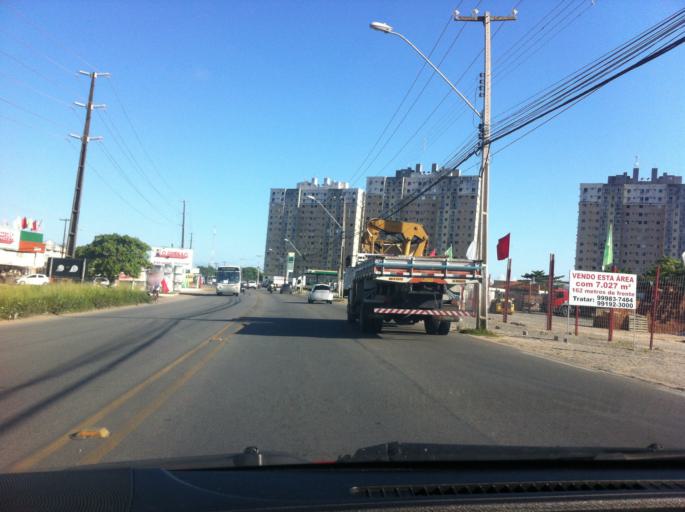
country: BR
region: Alagoas
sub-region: Maceio
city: Maceio
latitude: -9.5839
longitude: -35.7346
